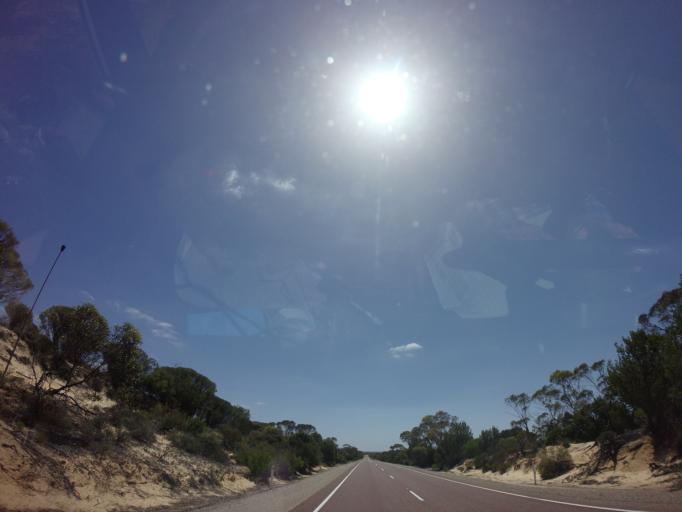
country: AU
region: South Australia
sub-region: Kimba
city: Caralue
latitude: -33.2195
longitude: 136.3411
